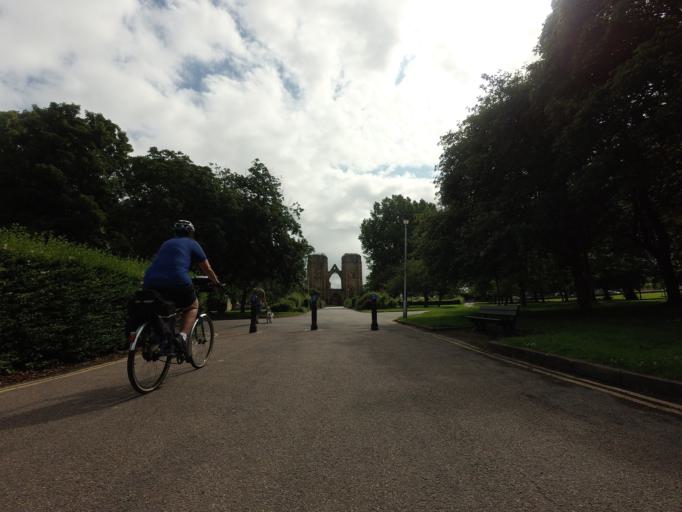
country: GB
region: Scotland
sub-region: Moray
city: Elgin
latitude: 57.6506
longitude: -3.3083
